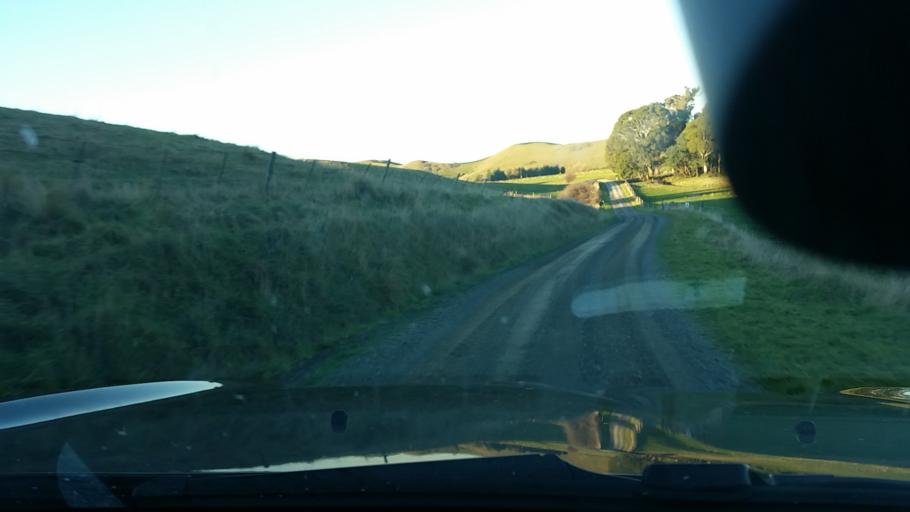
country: NZ
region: Marlborough
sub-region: Marlborough District
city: Blenheim
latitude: -41.7489
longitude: 174.0710
